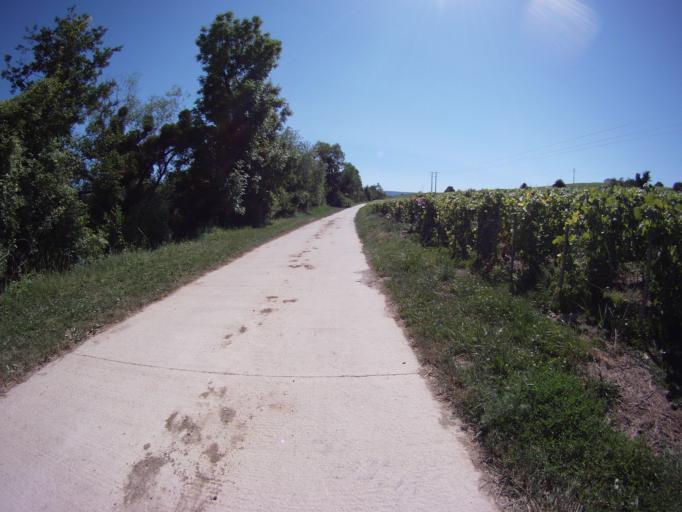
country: FR
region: Champagne-Ardenne
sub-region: Departement de la Marne
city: Dormans
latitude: 49.0894
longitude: 3.6441
